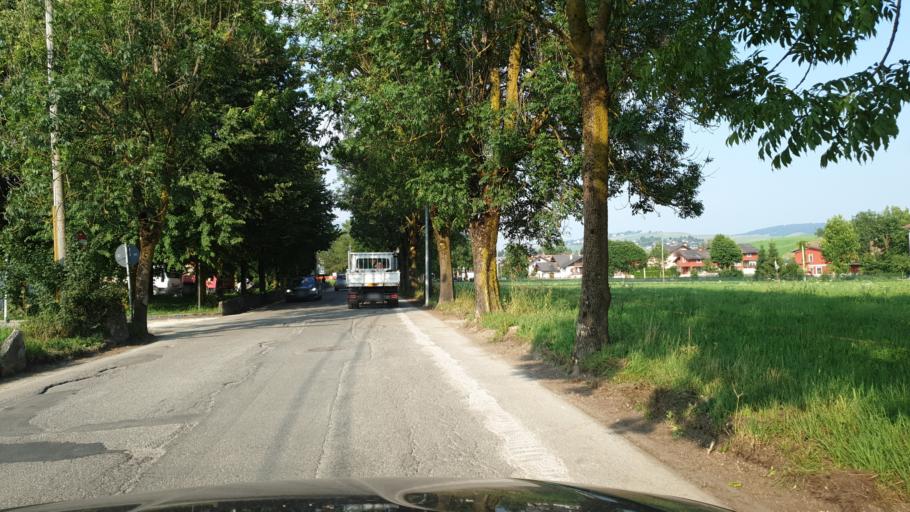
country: IT
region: Veneto
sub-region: Provincia di Vicenza
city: Asiago
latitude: 45.8667
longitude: 11.5035
